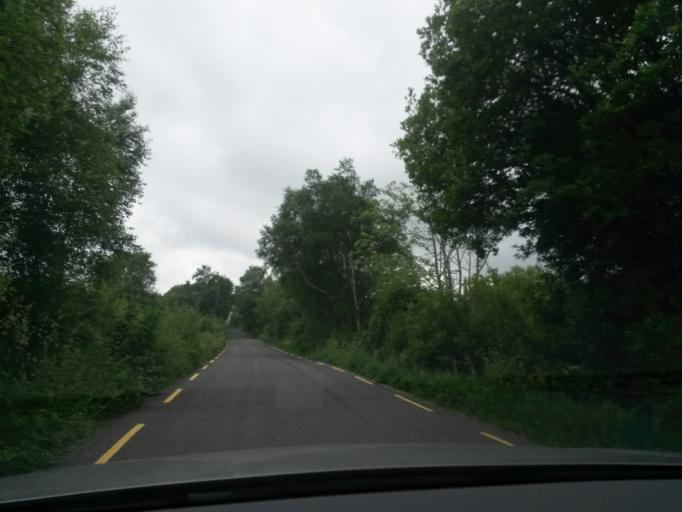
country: IE
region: Munster
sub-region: Ciarrai
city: Killorglin
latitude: 51.9956
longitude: -9.8552
